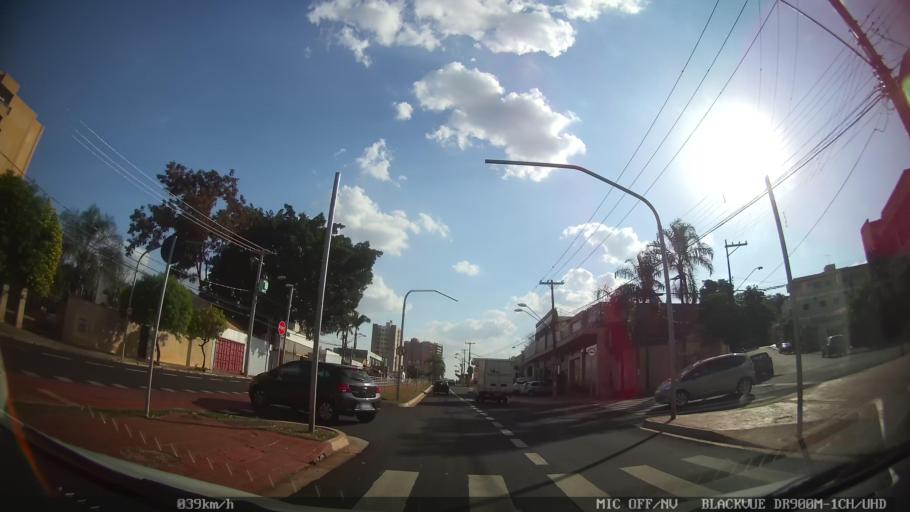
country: BR
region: Sao Paulo
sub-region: Ribeirao Preto
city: Ribeirao Preto
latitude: -21.1747
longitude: -47.8349
